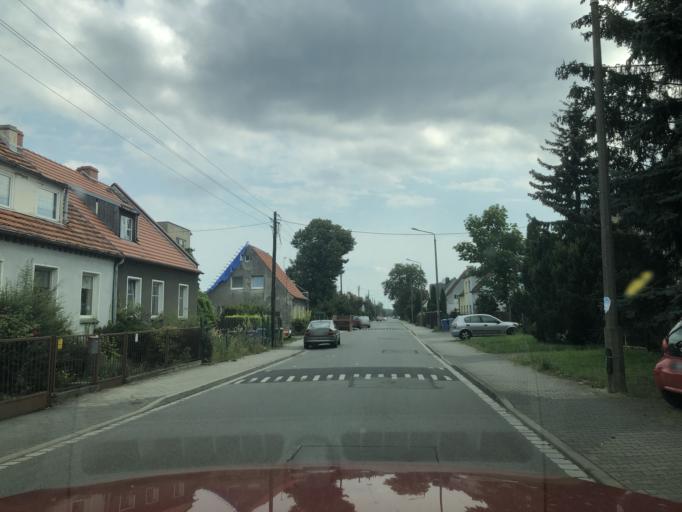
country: PL
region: Lower Silesian Voivodeship
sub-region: Powiat wroclawski
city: Smolec
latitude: 51.1581
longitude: 16.9054
